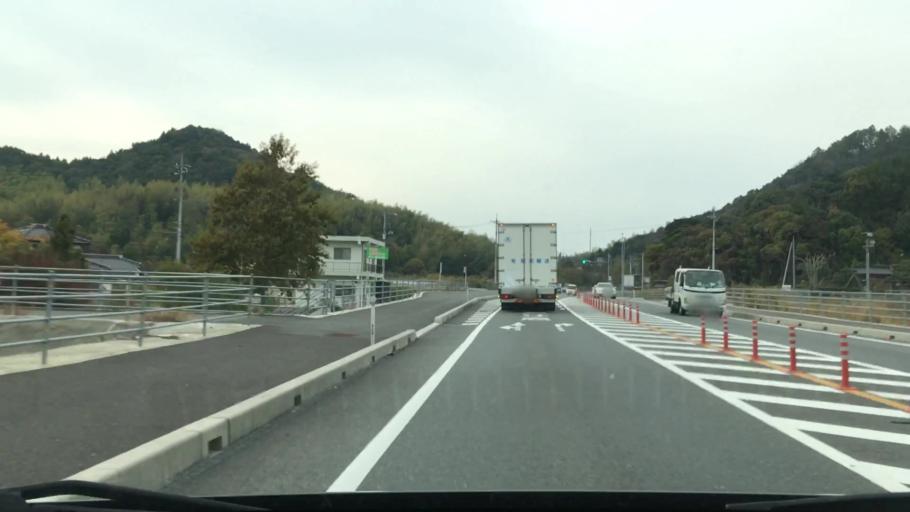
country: JP
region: Yamaguchi
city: Hofu
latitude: 34.0646
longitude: 131.4832
